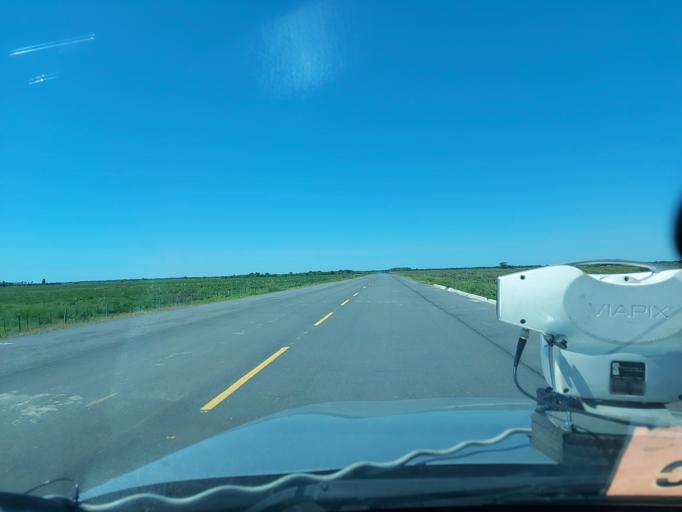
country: PY
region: Neembucu
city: Pilar
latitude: -26.8389
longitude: -58.2294
